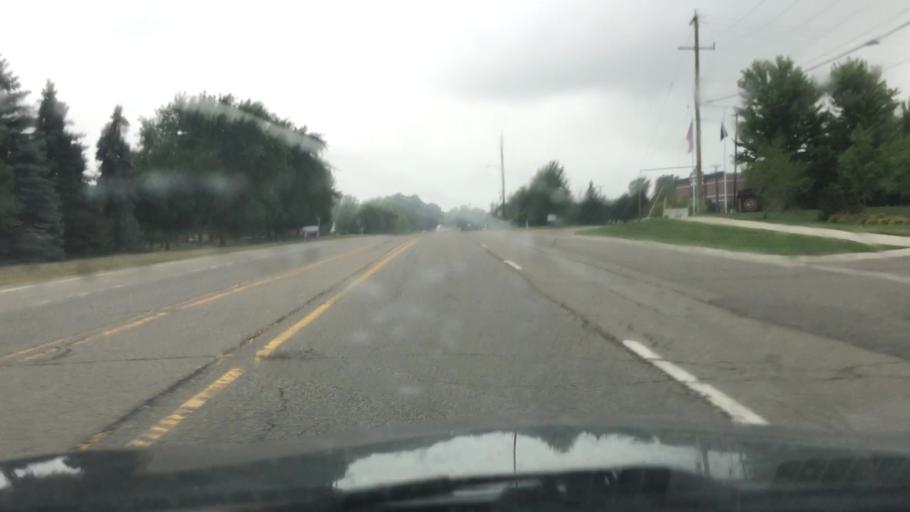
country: US
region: Michigan
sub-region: Oakland County
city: Wixom
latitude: 42.5241
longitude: -83.5477
